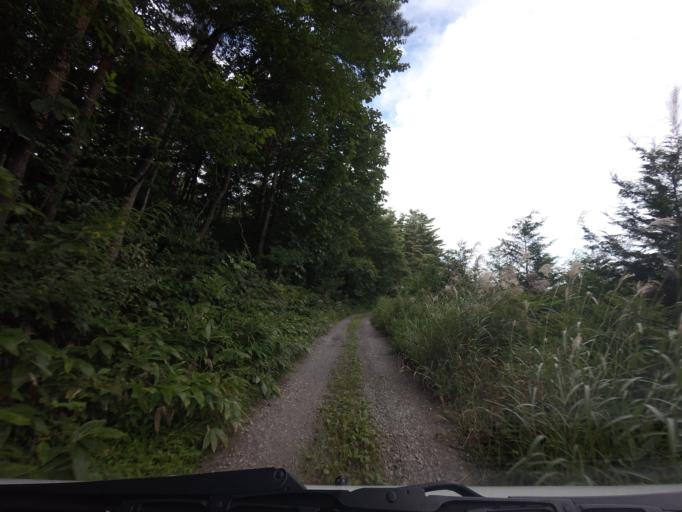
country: JP
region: Fukushima
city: Nihommatsu
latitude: 37.6023
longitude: 140.3447
